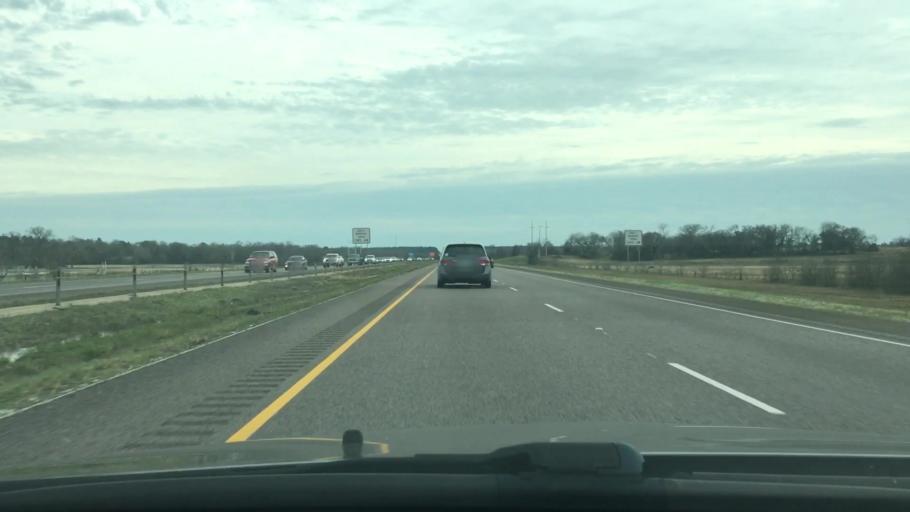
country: US
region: Texas
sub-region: Madison County
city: Madisonville
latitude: 30.9040
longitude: -95.7851
